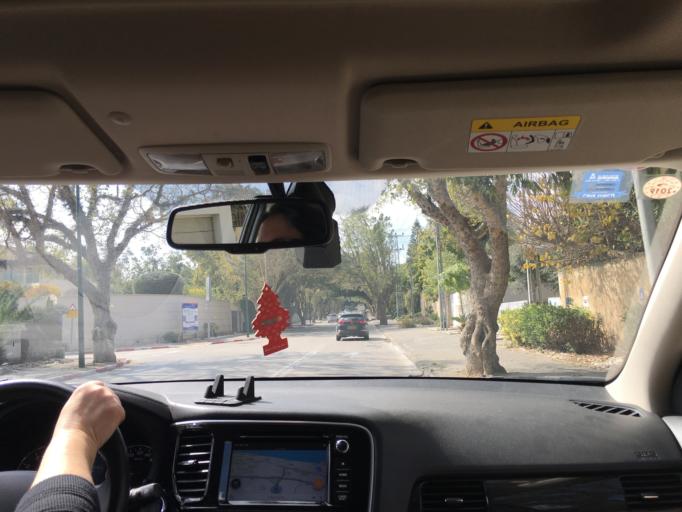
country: IL
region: Tel Aviv
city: Kefar Shemaryahu
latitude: 32.1804
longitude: 34.8143
